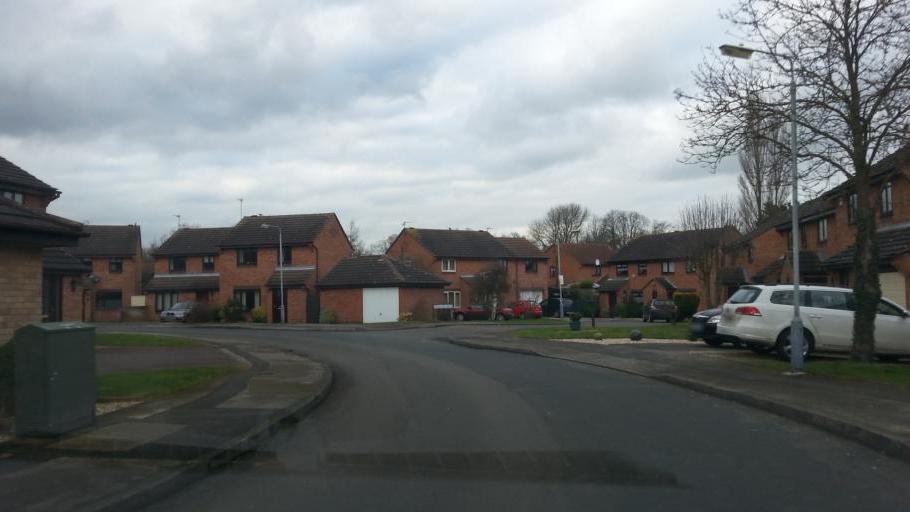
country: GB
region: England
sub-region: Nottinghamshire
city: Newark on Trent
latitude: 53.0757
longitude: -0.7763
